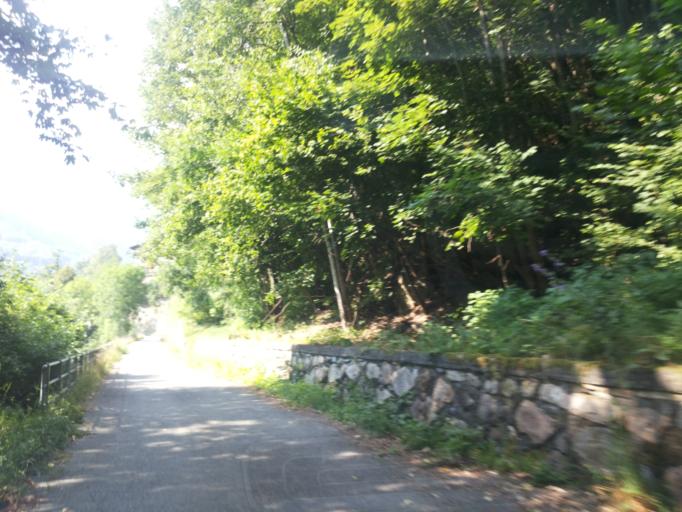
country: IT
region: Aosta Valley
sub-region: Valle d'Aosta
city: Fontainemore
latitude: 45.6437
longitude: 7.8638
